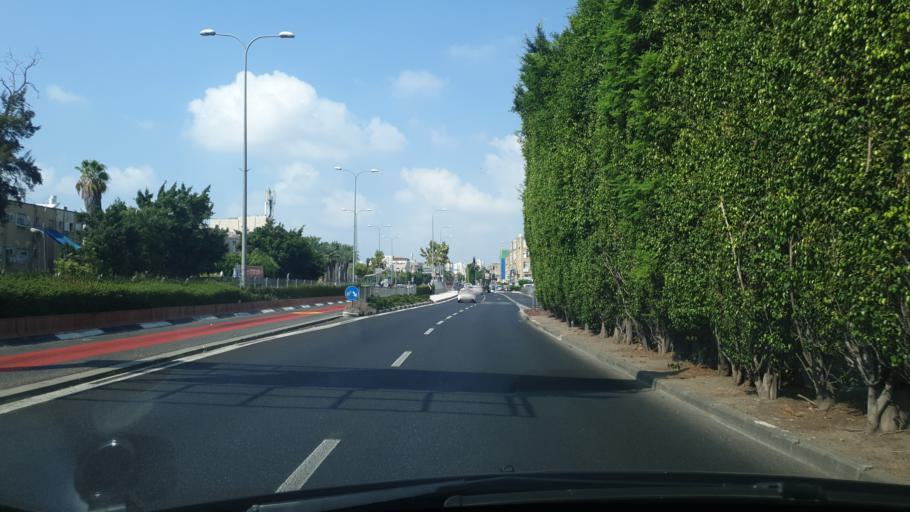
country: IL
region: Haifa
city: Qiryat Bialik
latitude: 32.8225
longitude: 35.0796
